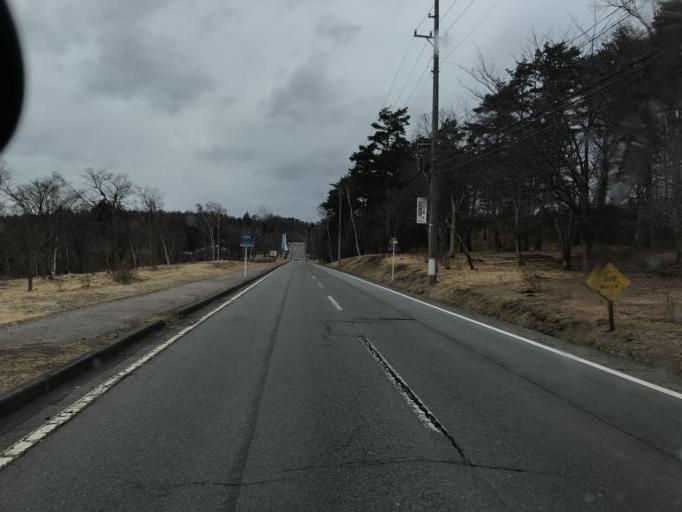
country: JP
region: Nagano
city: Chino
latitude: 35.9133
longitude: 138.3077
